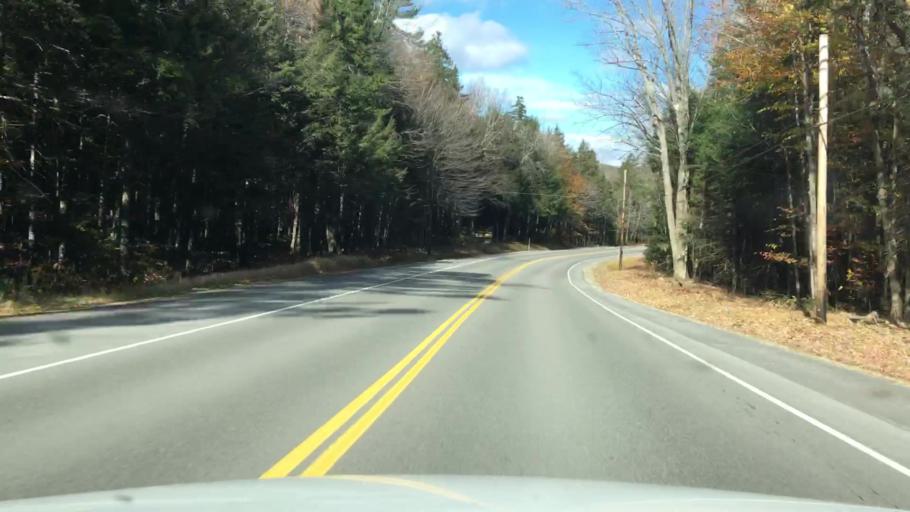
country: US
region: New Hampshire
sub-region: Coos County
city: Gorham
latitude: 44.3472
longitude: -71.1954
